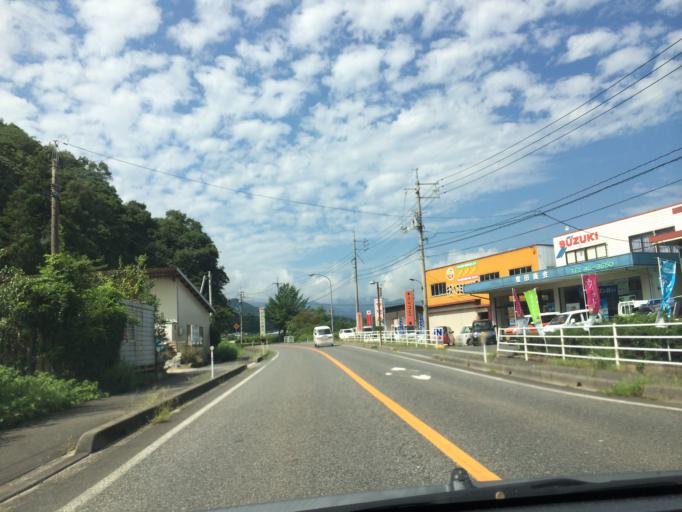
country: JP
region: Tottori
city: Kurayoshi
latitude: 35.3686
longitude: 133.7641
